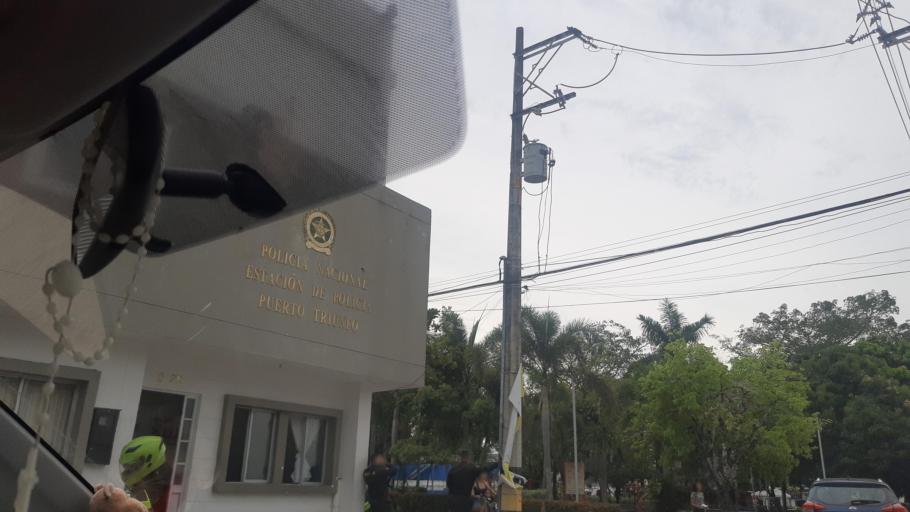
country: CO
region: Antioquia
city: Puerto Triunfo
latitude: 5.8696
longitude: -74.6412
